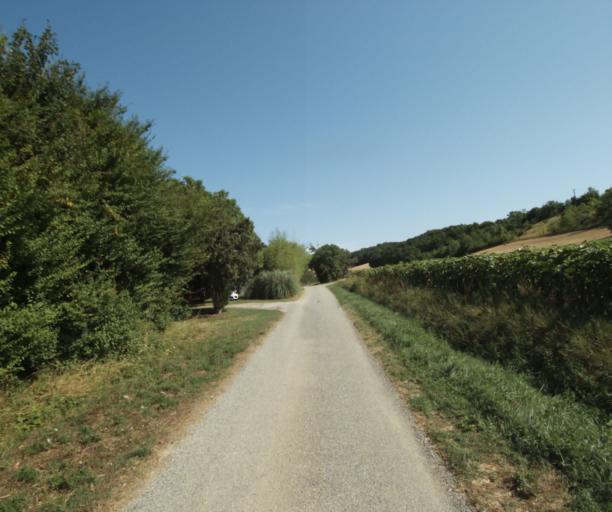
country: FR
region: Midi-Pyrenees
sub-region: Departement de la Haute-Garonne
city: Saint-Felix-Lauragais
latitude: 43.4458
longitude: 1.8414
